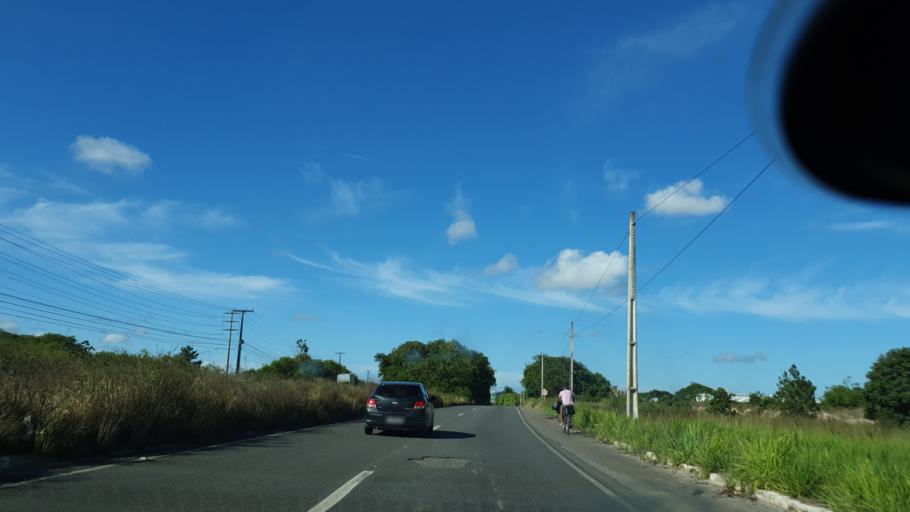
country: BR
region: Bahia
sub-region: Camacari
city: Camacari
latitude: -12.6788
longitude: -38.3019
